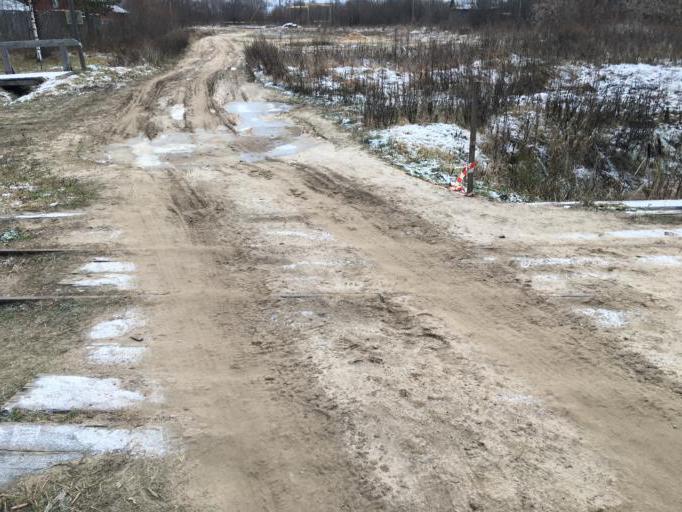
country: RU
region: Kostroma
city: Shar'ya
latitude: 58.3826
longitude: 45.4932
